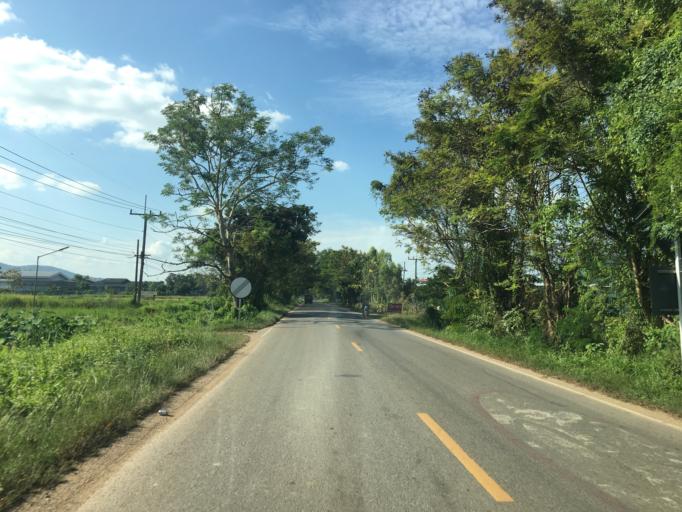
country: TH
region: Phayao
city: Chun
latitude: 19.3284
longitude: 100.1429
